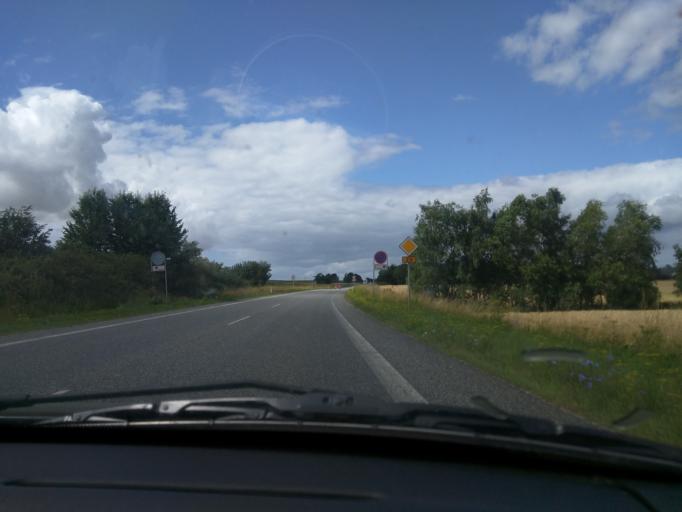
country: DK
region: Zealand
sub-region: Kalundborg Kommune
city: Svebolle
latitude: 55.6638
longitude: 11.2569
